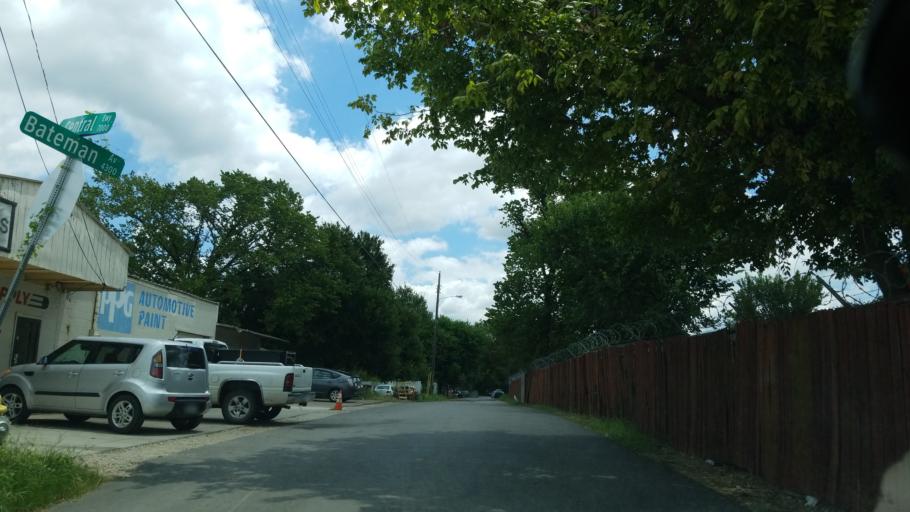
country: US
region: Texas
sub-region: Dallas County
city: Dallas
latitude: 32.7234
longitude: -96.7581
